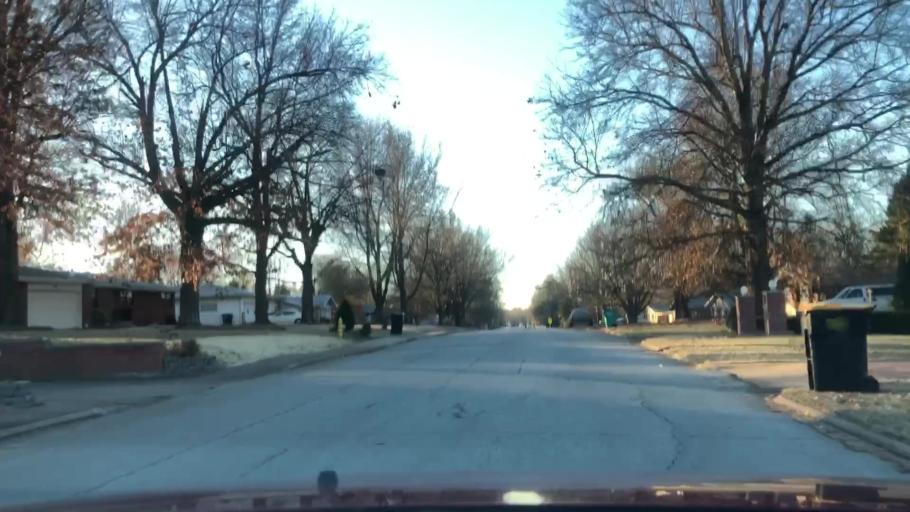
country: US
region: Missouri
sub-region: Greene County
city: Springfield
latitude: 37.1790
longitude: -93.2435
